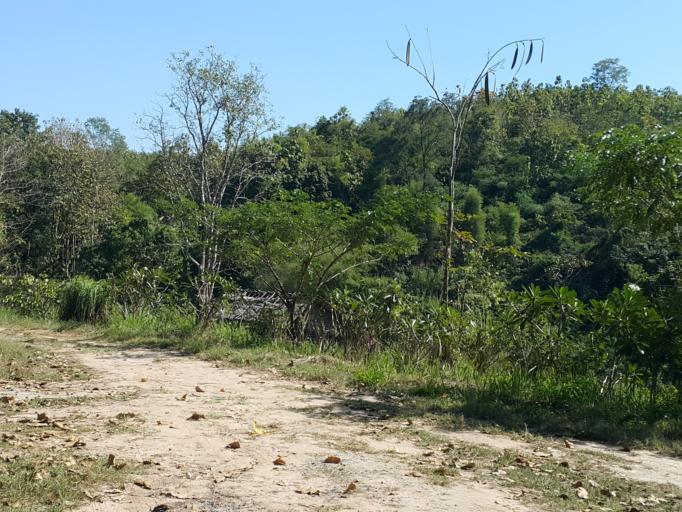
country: TH
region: Chiang Mai
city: Mae Taeng
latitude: 18.9553
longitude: 98.9048
